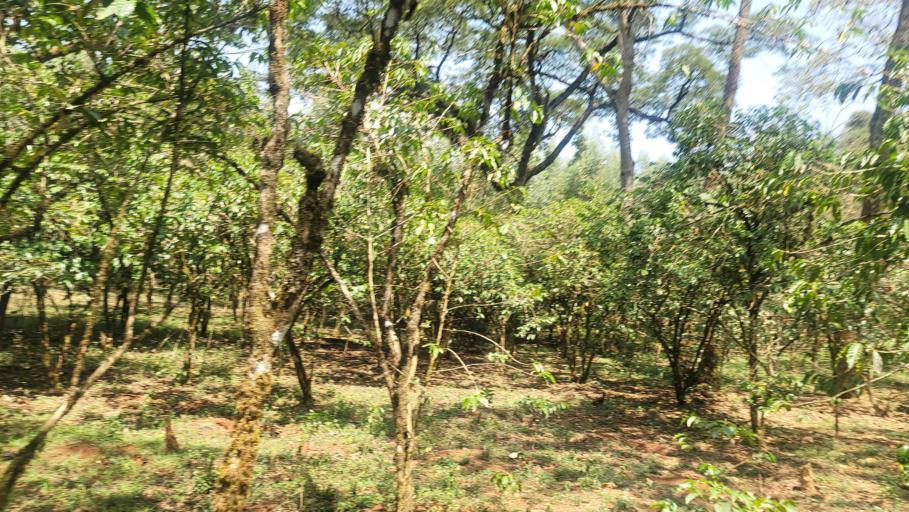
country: ET
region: Oromiya
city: Agaro
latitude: 7.7966
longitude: 36.4883
